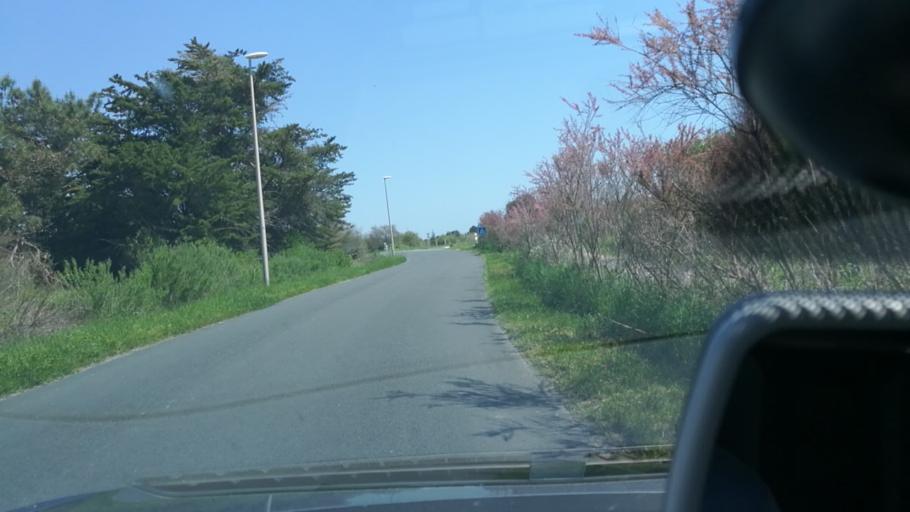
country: FR
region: Poitou-Charentes
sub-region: Departement de la Charente-Maritime
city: Saint-Trojan-les-Bains
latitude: 45.8635
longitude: -1.2296
